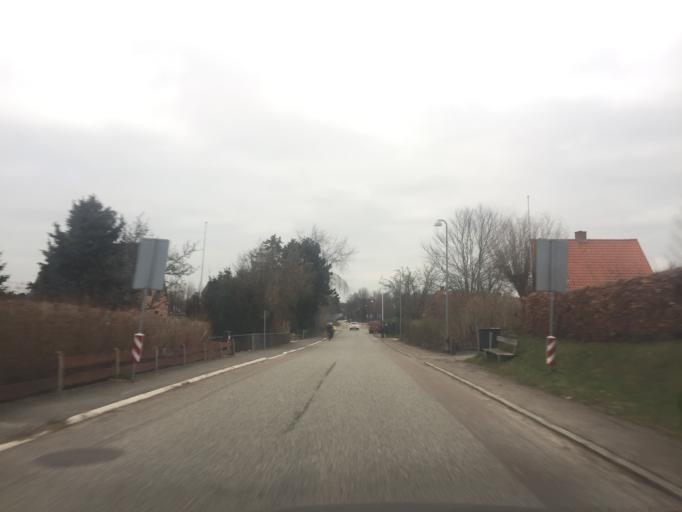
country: DK
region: Capital Region
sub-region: Halsnaes Kommune
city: Liseleje
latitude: 55.9981
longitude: 11.9730
